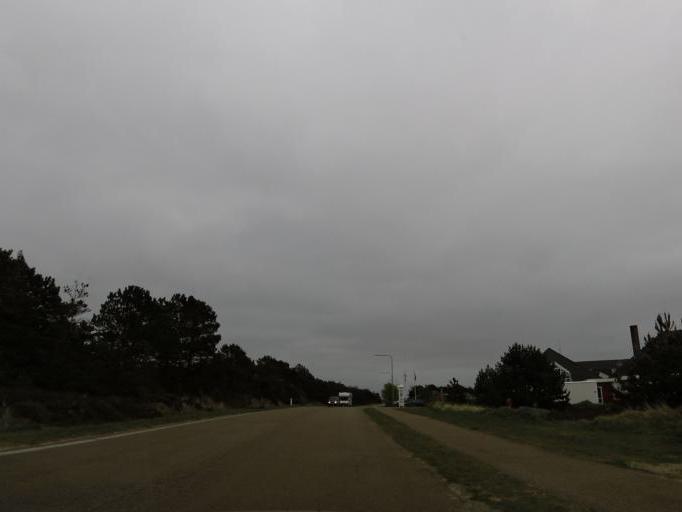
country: DE
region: Schleswig-Holstein
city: List
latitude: 55.0880
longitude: 8.5465
